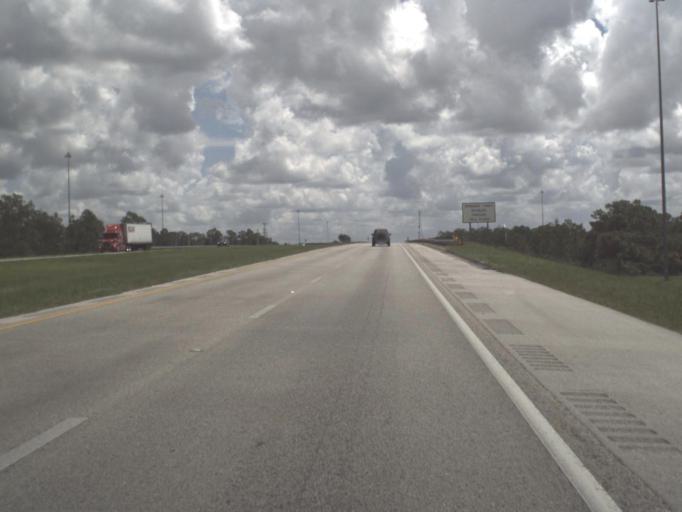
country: US
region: Florida
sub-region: Collier County
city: Golden Gate
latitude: 26.1612
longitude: -81.6903
